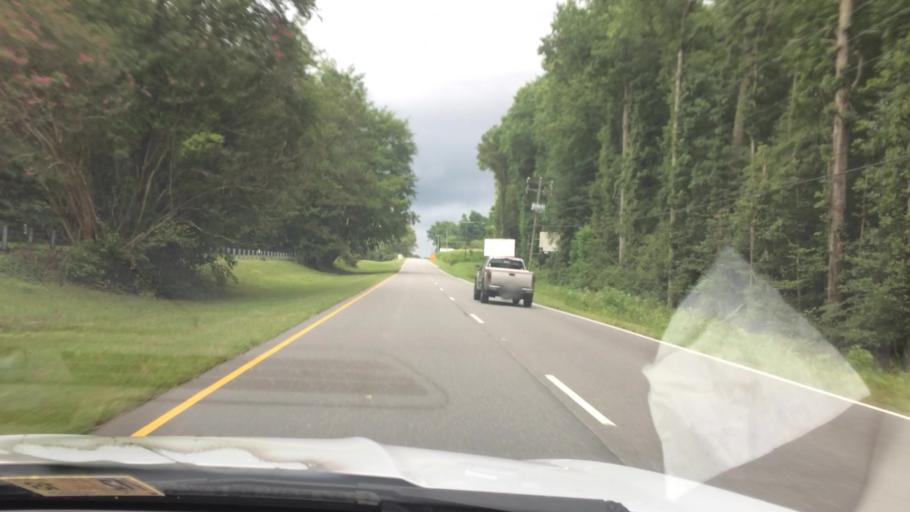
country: US
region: Virginia
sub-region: King William County
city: West Point
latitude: 37.4030
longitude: -76.8229
